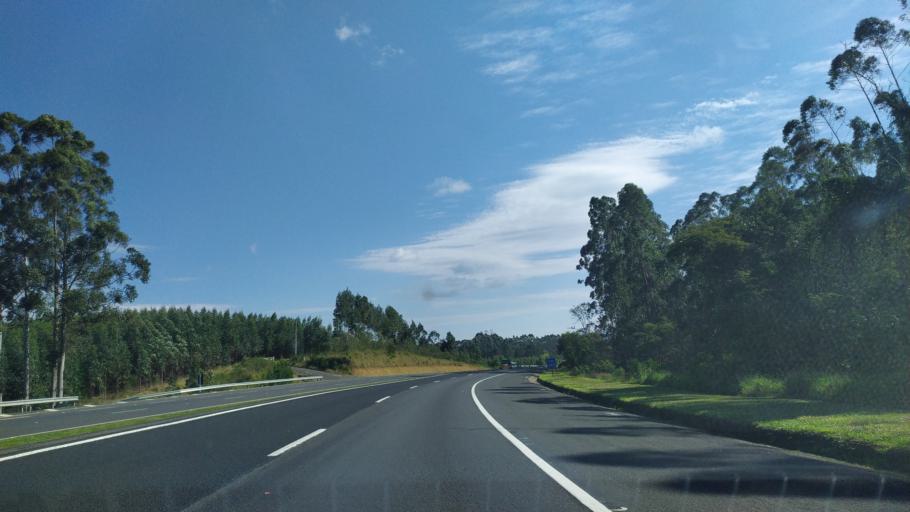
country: BR
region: Parana
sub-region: Telemaco Borba
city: Telemaco Borba
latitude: -24.4255
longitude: -50.7695
